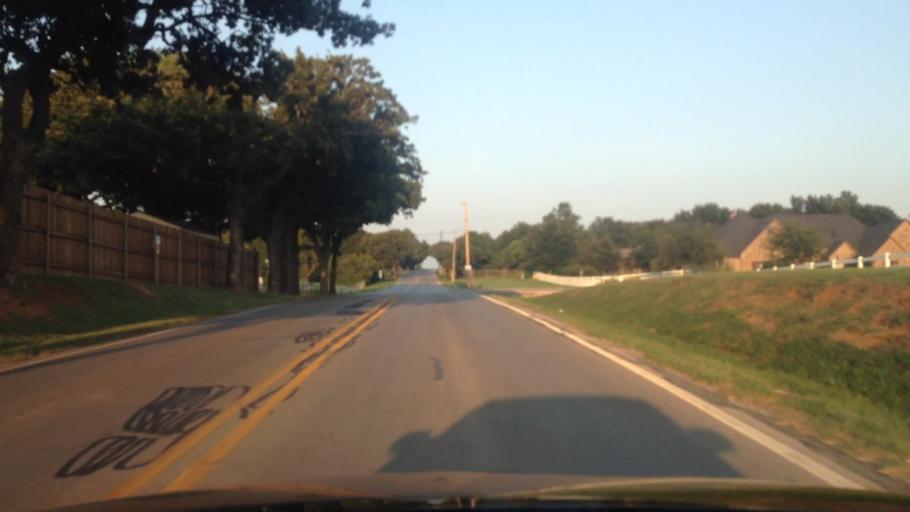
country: US
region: Texas
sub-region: Tarrant County
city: Kennedale
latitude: 32.6070
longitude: -97.2088
